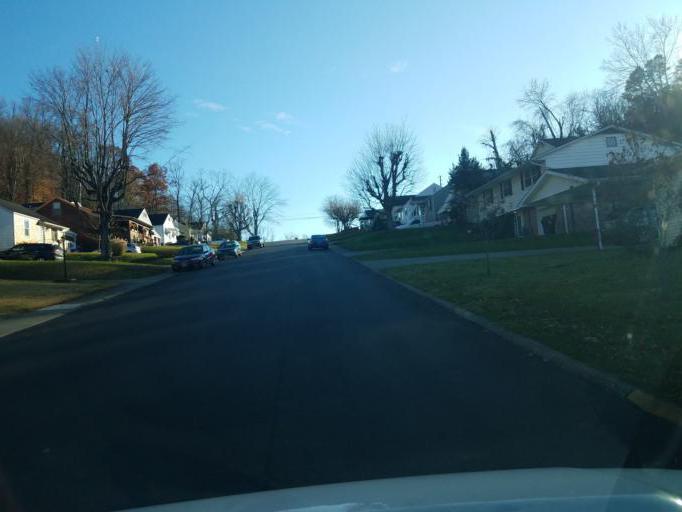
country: US
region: Ohio
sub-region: Scioto County
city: Portsmouth
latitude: 38.7557
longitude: -82.9861
